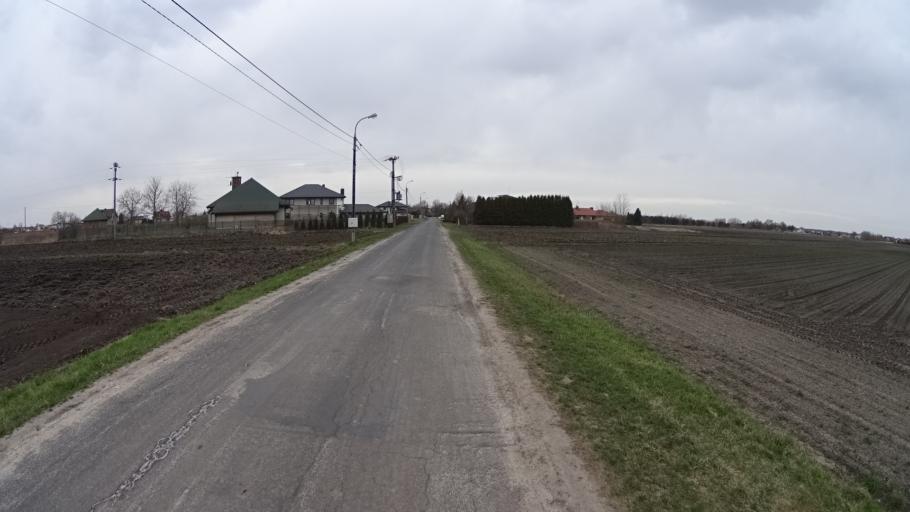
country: PL
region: Masovian Voivodeship
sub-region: Powiat warszawski zachodni
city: Ozarow Mazowiecki
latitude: 52.2455
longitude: 20.7509
